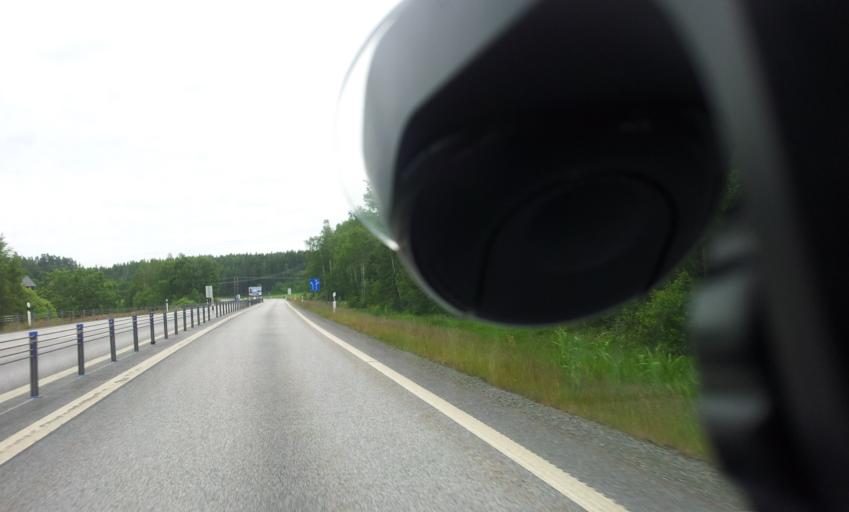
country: SE
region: OEstergoetland
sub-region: Valdemarsviks Kommun
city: Valdemarsvik
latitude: 58.1967
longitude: 16.5471
